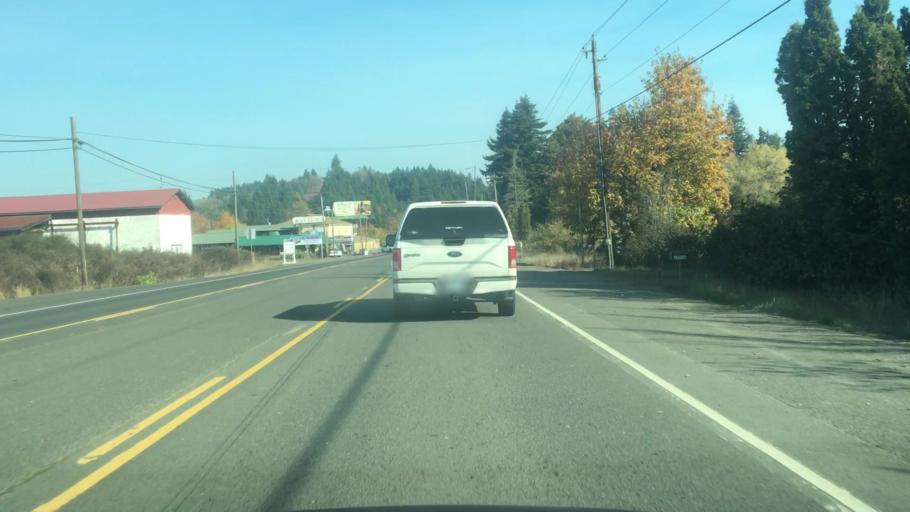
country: US
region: Oregon
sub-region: Polk County
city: Grand Ronde
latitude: 45.0588
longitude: -123.6117
